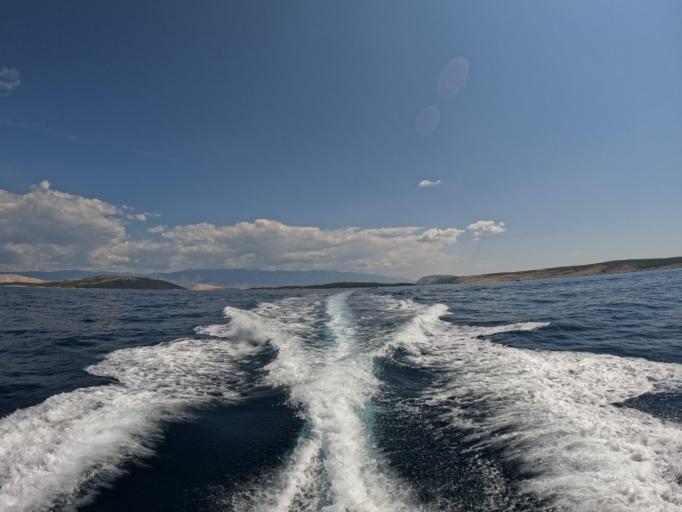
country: HR
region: Primorsko-Goranska
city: Lopar
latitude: 44.8613
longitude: 14.6935
